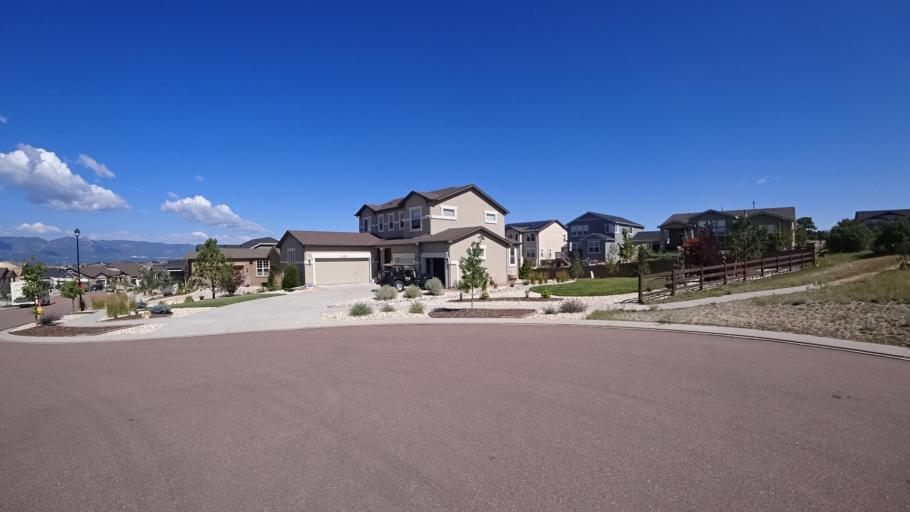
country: US
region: Colorado
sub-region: El Paso County
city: Black Forest
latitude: 38.9779
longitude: -104.7412
